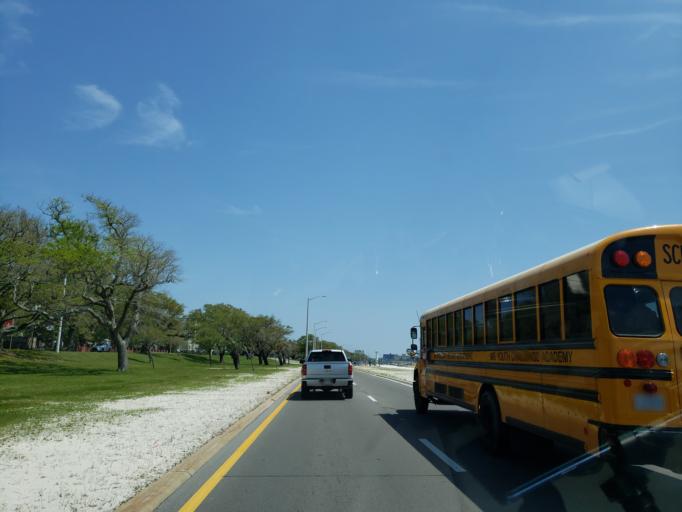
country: US
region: Mississippi
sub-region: Harrison County
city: Biloxi
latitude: 30.3946
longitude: -88.9086
